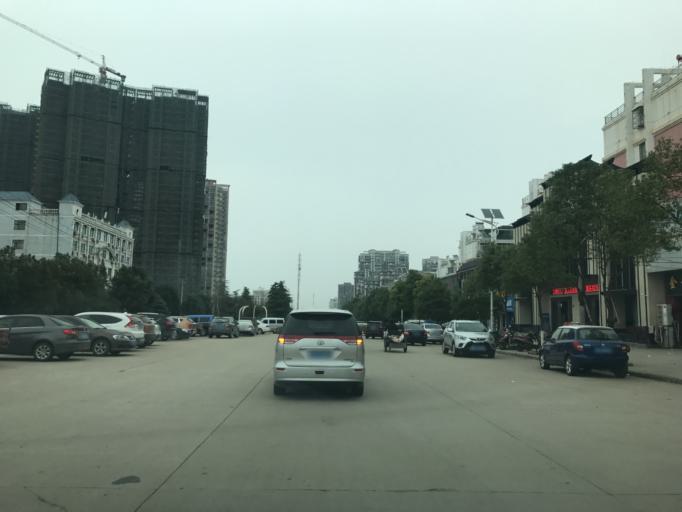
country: CN
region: Hubei
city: Anlu
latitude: 31.2648
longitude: 113.7044
